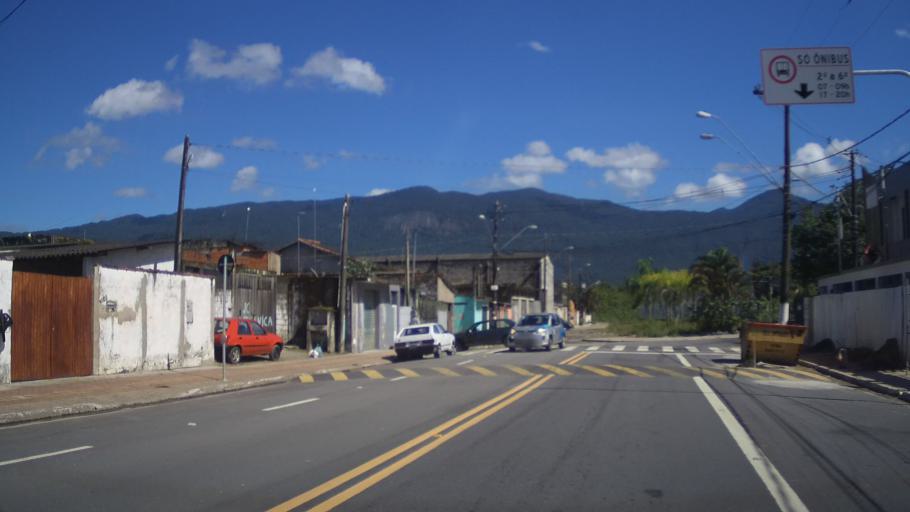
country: BR
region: Sao Paulo
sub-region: Mongagua
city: Mongagua
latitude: -24.0301
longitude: -46.5353
